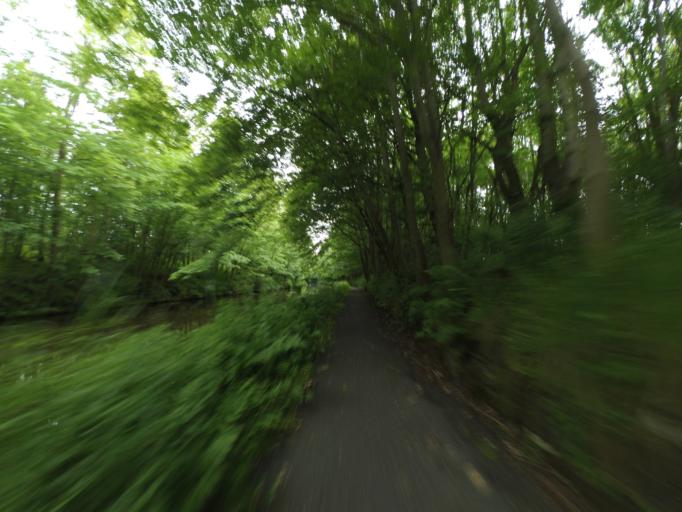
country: GB
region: Scotland
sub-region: West Lothian
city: Broxburn
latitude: 55.9700
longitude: -3.4779
